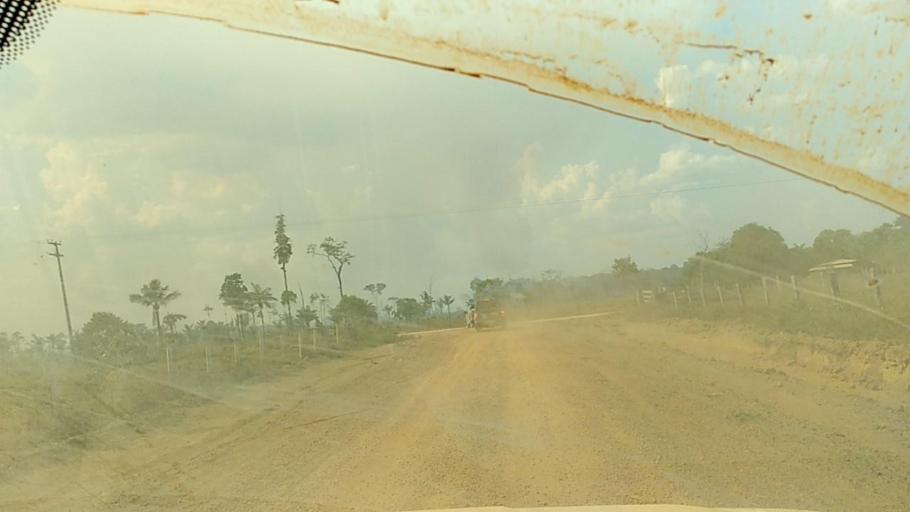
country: BR
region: Rondonia
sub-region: Porto Velho
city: Porto Velho
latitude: -8.6840
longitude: -63.2393
